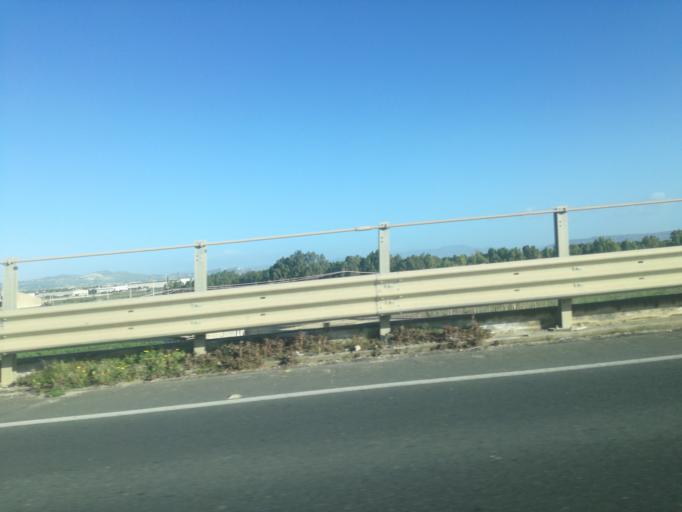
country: IT
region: Sicily
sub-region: Provincia di Caltanissetta
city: Gela
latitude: 37.0605
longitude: 14.2780
